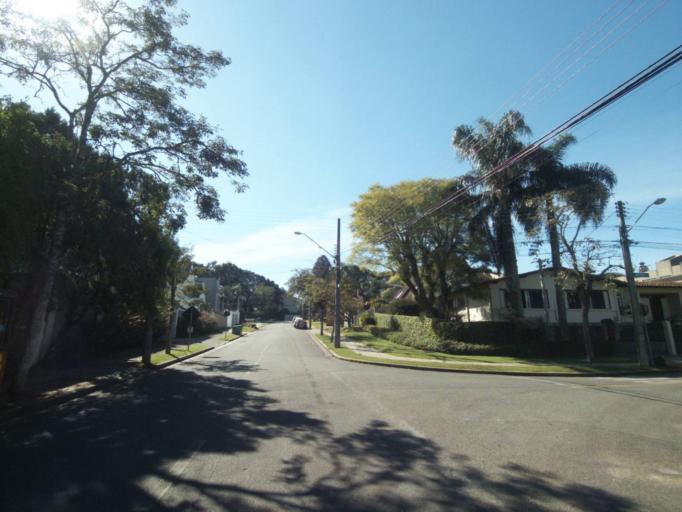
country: BR
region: Parana
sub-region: Curitiba
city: Curitiba
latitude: -25.4139
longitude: -49.2349
